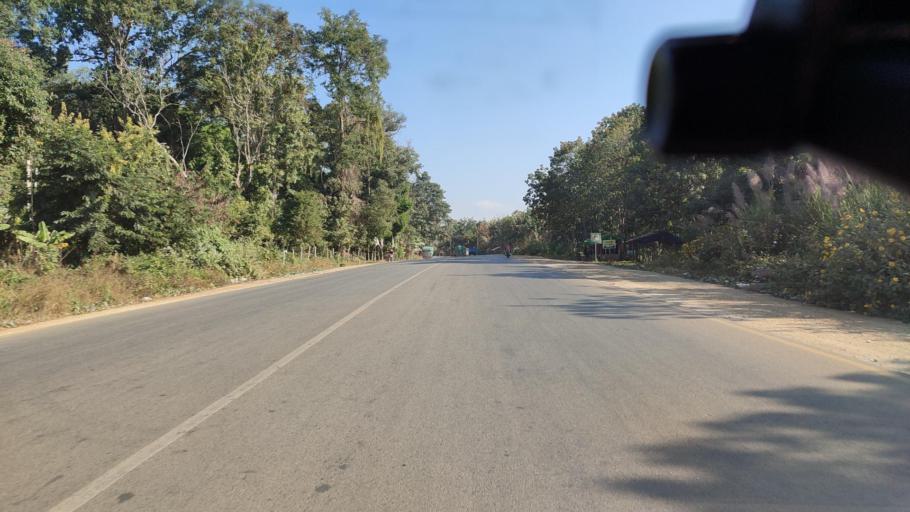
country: MM
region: Shan
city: Lashio
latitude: 23.2427
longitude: 97.9197
